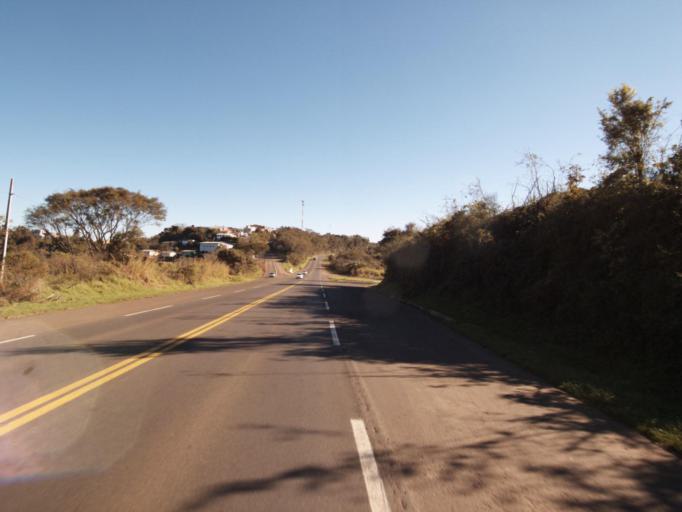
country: BR
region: Santa Catarina
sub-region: Chapeco
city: Chapeco
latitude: -26.9820
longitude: -52.5971
